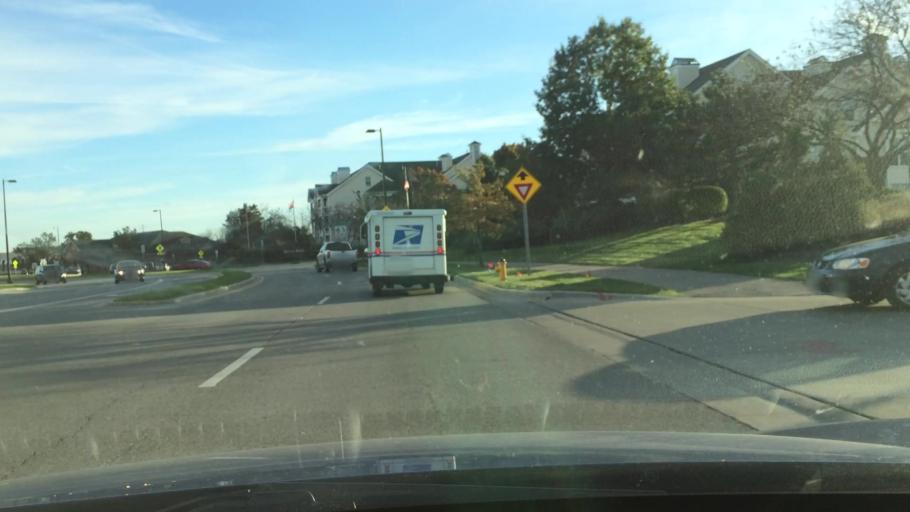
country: US
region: Ohio
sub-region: Franklin County
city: Dublin
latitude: 40.0786
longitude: -83.1420
